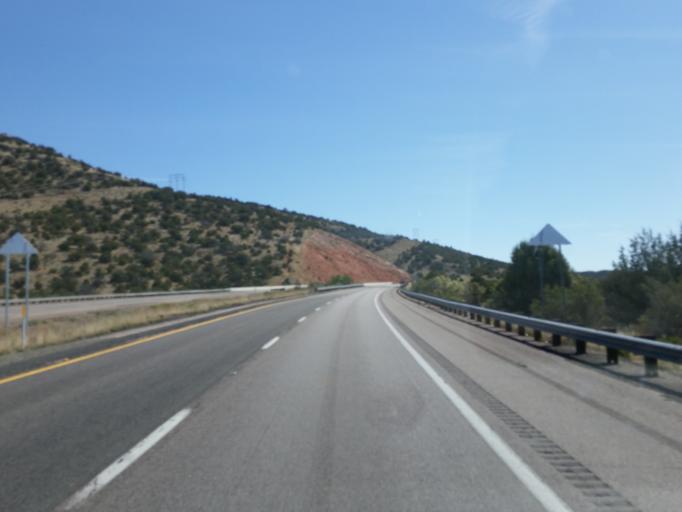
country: US
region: Arizona
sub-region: Mohave County
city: Peach Springs
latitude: 35.2846
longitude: -113.1227
